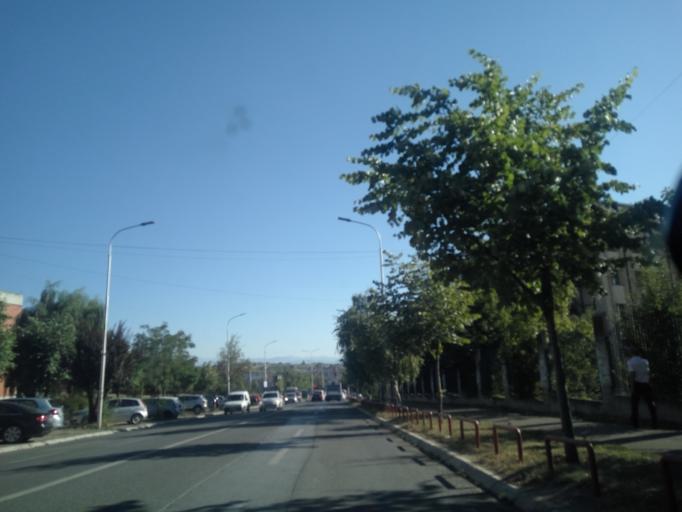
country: XK
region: Pristina
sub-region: Komuna e Prishtines
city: Pristina
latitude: 42.6515
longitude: 21.1657
